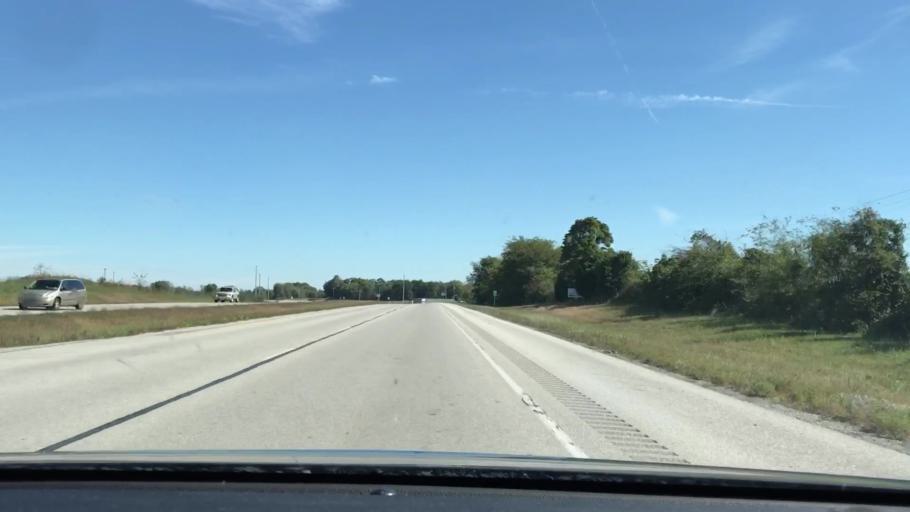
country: US
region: Kentucky
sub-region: Logan County
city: Auburn
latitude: 36.8955
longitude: -86.6004
